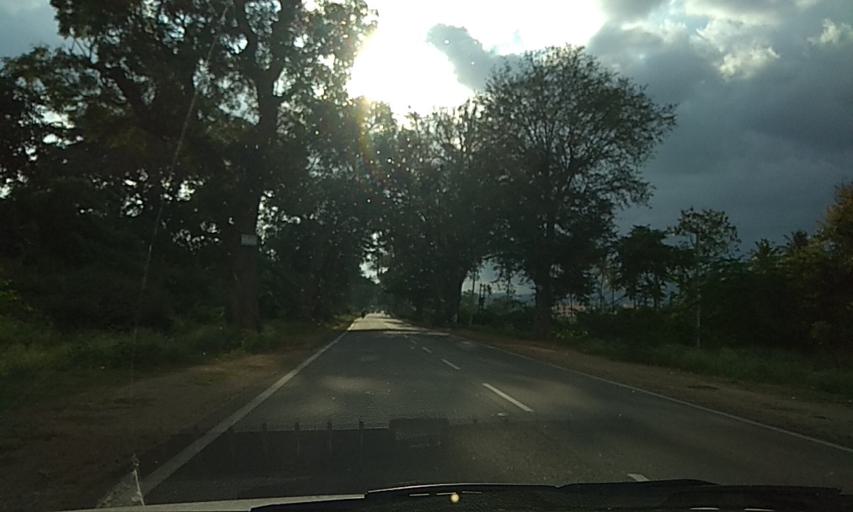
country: IN
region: Karnataka
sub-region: Chamrajnagar
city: Gundlupet
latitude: 11.8108
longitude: 76.7109
